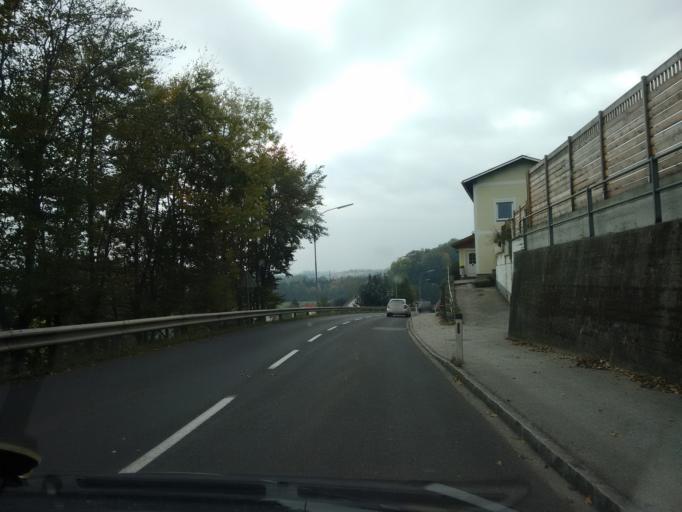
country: AT
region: Upper Austria
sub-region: Politischer Bezirk Steyr-Land
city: Bad Hall
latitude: 48.0555
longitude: 14.2005
